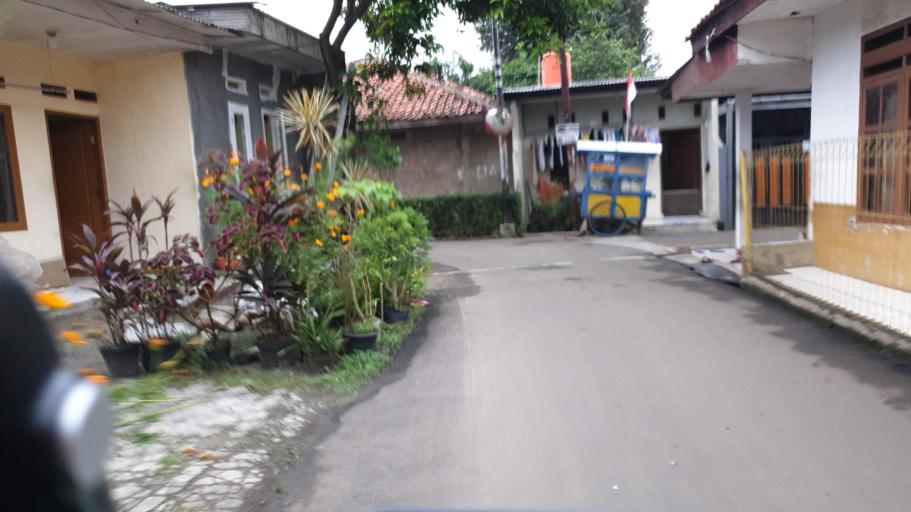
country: ID
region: West Java
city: Pamulang
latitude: -6.3291
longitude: 106.7731
